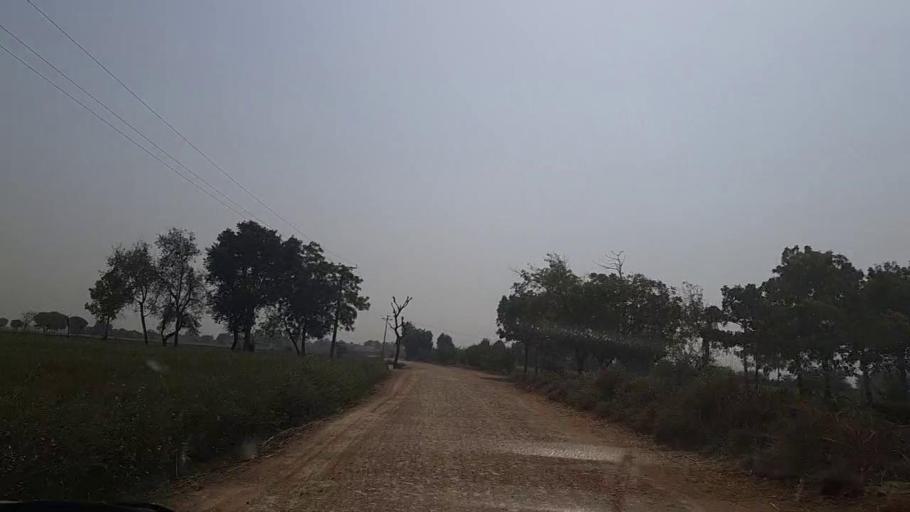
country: PK
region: Sindh
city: Pithoro
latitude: 25.5530
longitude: 69.2484
